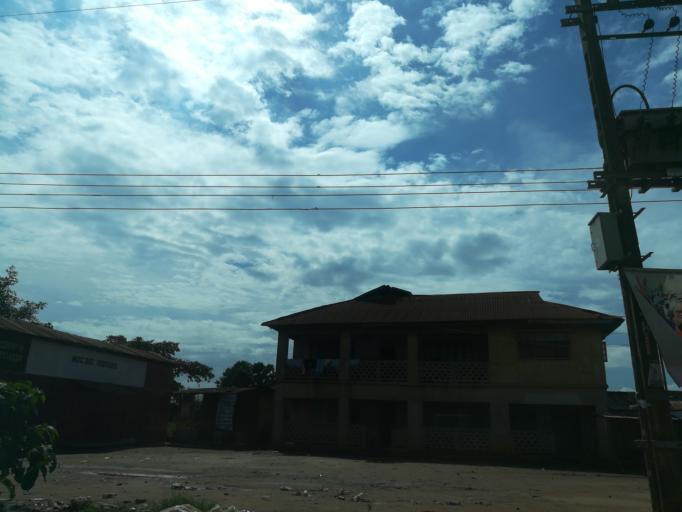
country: NG
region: Lagos
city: Ikorodu
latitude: 6.5973
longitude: 3.5179
